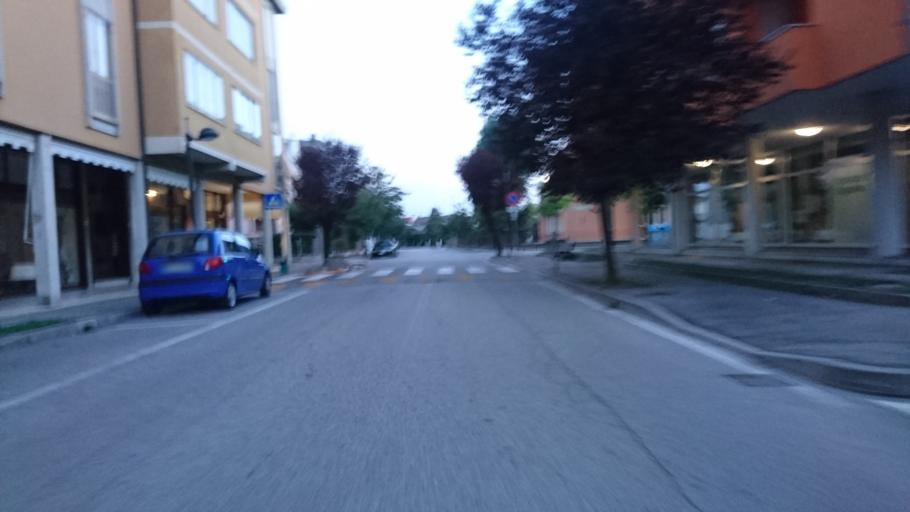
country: IT
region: Veneto
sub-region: Provincia di Padova
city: Abano Terme
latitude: 45.3663
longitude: 11.7935
